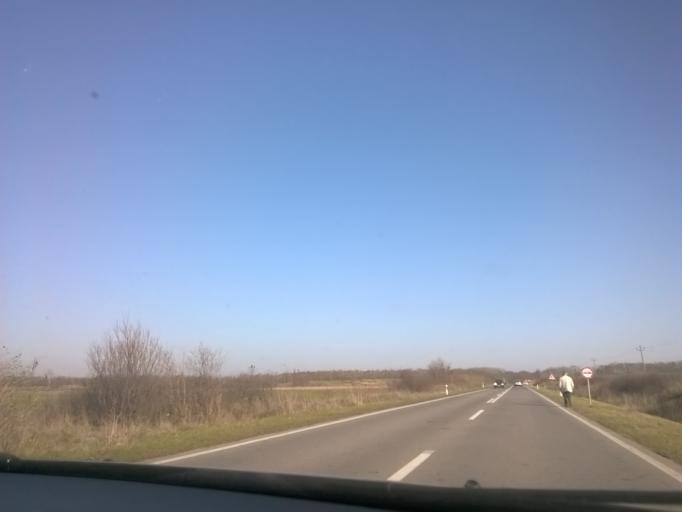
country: RS
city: Vlajkovac
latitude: 45.0657
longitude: 21.1883
